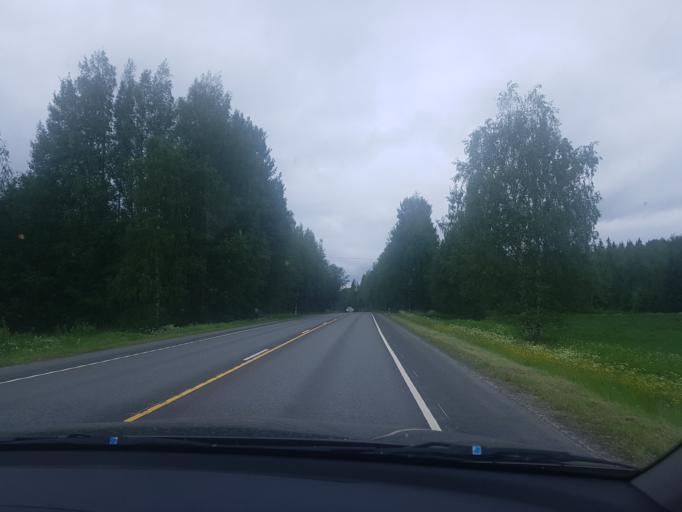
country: FI
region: Pirkanmaa
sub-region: Tampere
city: Paelkaene
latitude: 61.3948
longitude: 24.2121
